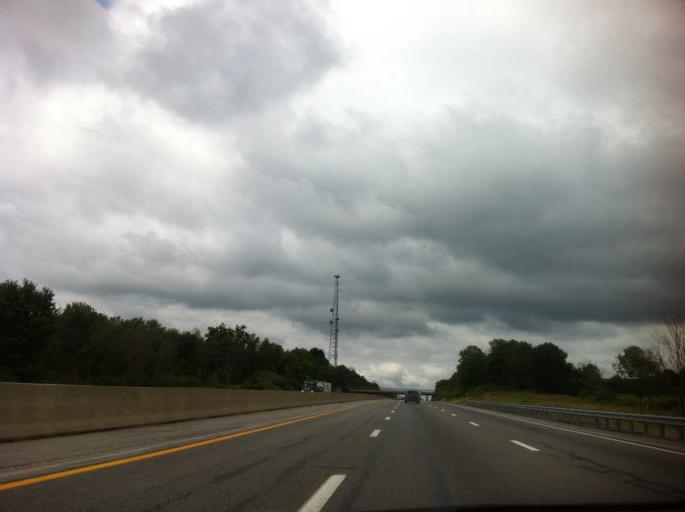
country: US
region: Ohio
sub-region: Portage County
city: Mantua
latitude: 41.2438
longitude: -81.2058
